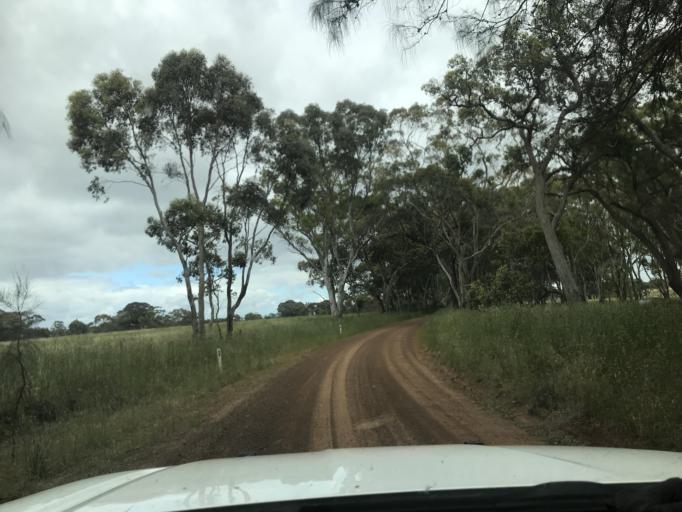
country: AU
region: South Australia
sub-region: Wattle Range
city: Penola
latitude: -37.1029
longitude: 141.2415
